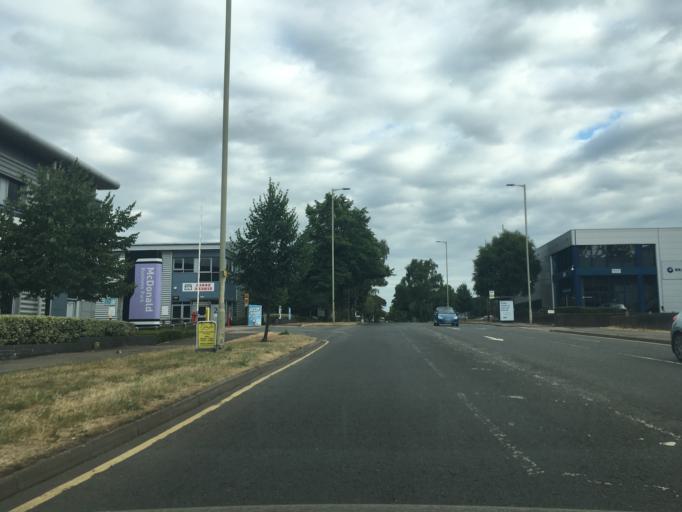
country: GB
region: England
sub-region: Hertfordshire
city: Hemel Hempstead
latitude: 51.7664
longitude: -0.4433
